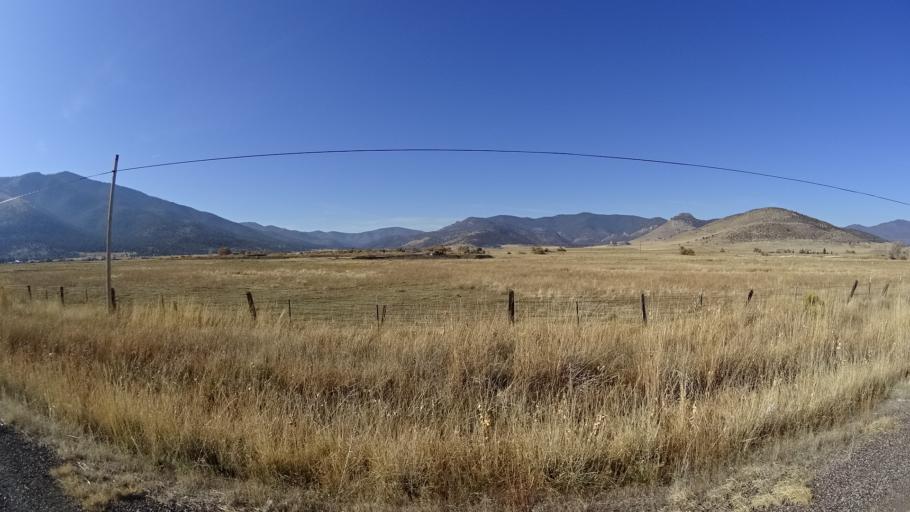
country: US
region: California
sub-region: Siskiyou County
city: Weed
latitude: 41.5052
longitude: -122.5163
